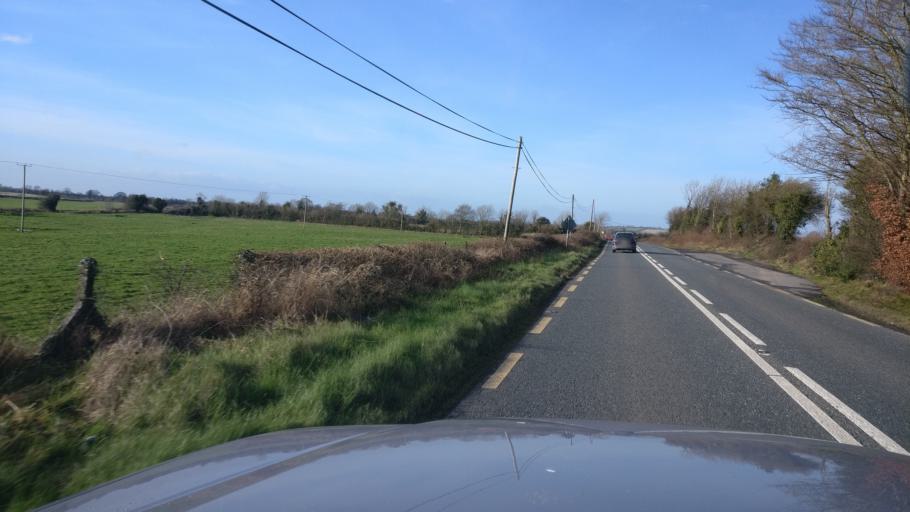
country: IE
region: Leinster
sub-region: Laois
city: Mountmellick
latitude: 53.1626
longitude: -7.3704
